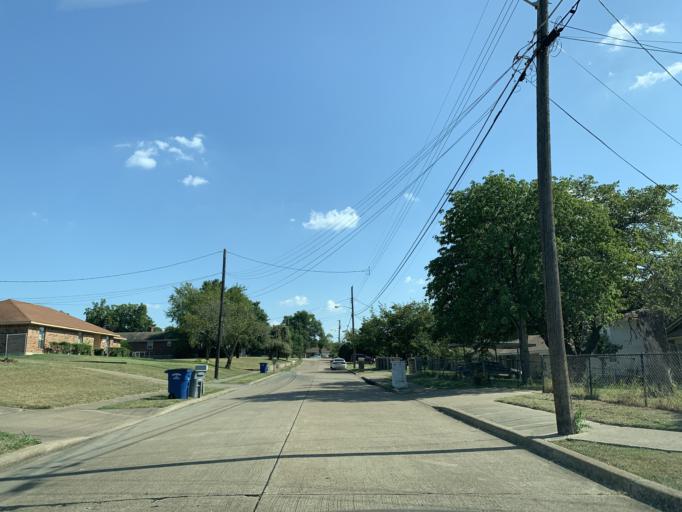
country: US
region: Texas
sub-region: Dallas County
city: Hutchins
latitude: 32.6565
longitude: -96.7798
